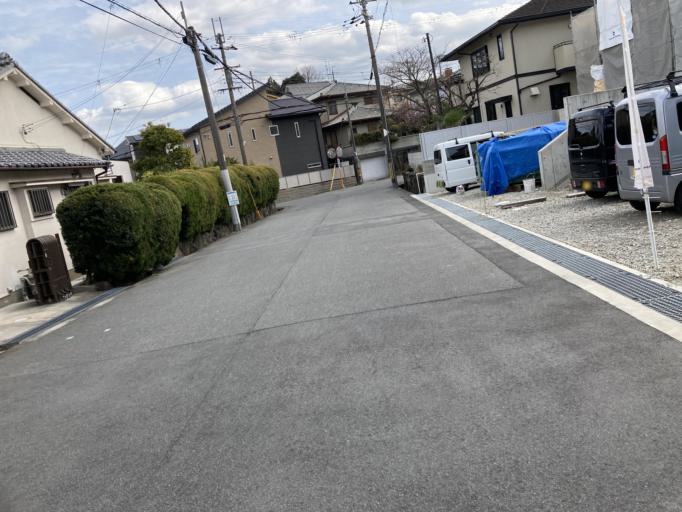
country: JP
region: Nara
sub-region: Ikoma-shi
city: Ikoma
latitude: 34.7027
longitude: 135.7035
